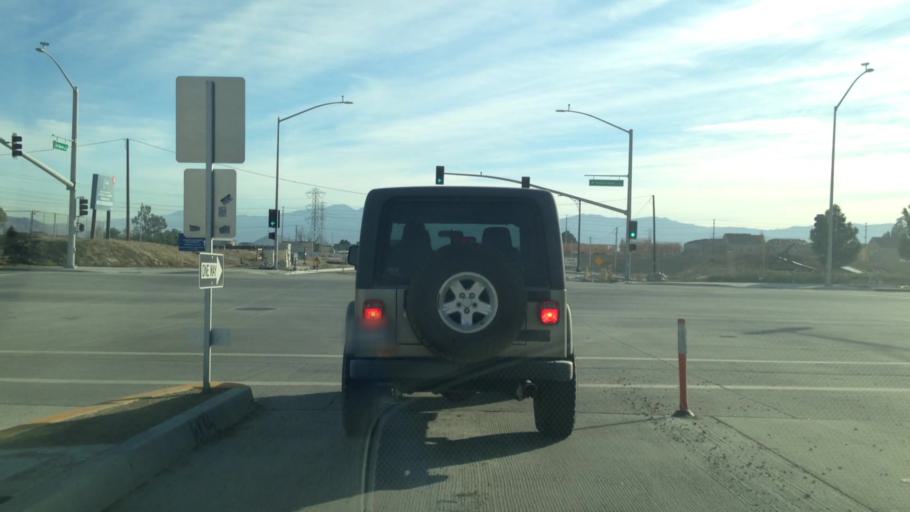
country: US
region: California
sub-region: Riverside County
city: Mira Loma
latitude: 34.0011
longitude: -117.5759
